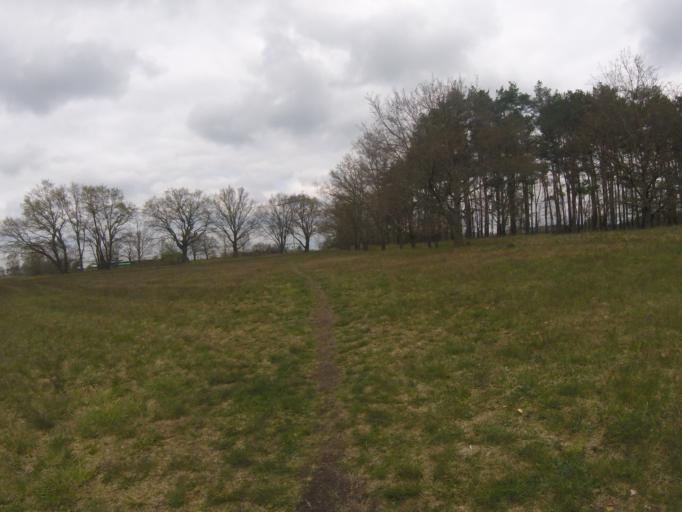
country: DE
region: Brandenburg
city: Mittenwalde
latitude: 52.2535
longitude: 13.5655
